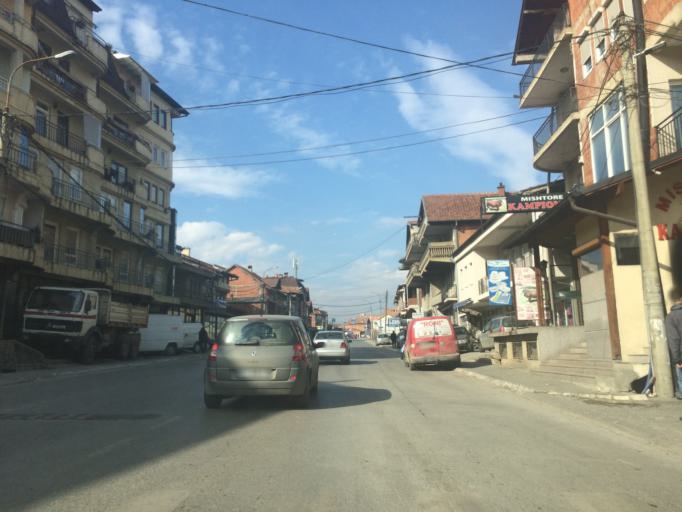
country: XK
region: Pristina
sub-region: Komuna e Prishtines
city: Pristina
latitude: 42.6800
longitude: 21.1603
